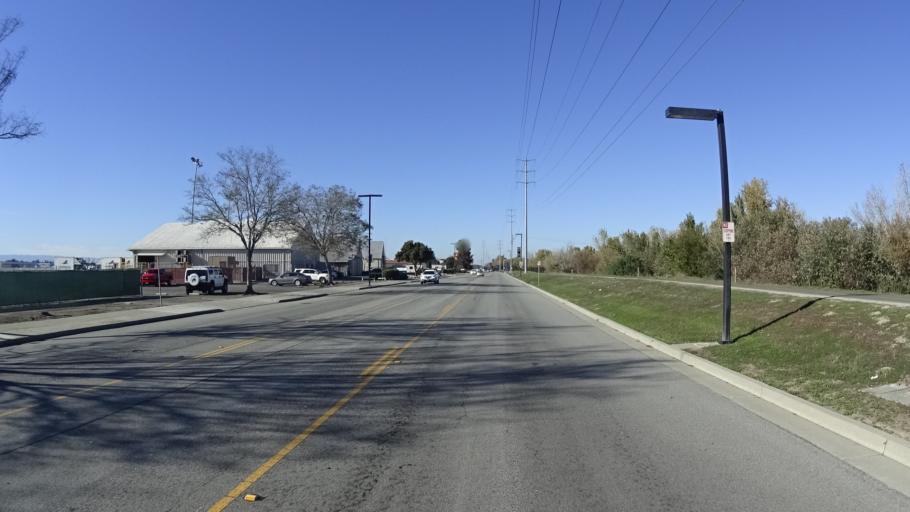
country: US
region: California
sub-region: Santa Clara County
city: San Jose
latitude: 37.3553
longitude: -121.9135
